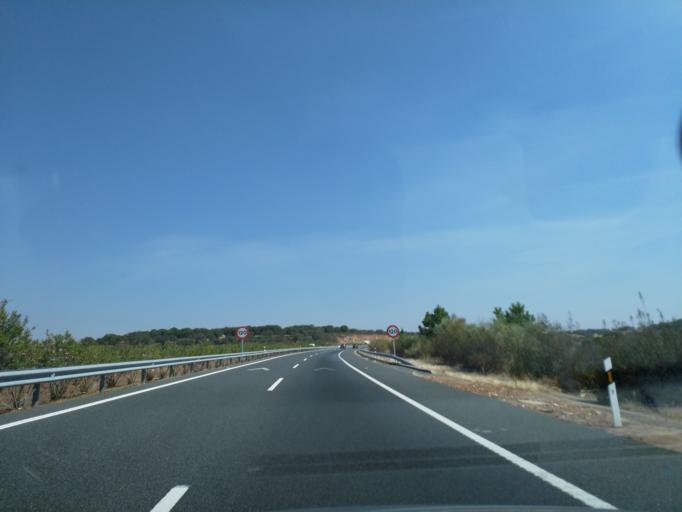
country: ES
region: Extremadura
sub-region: Provincia de Badajoz
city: Aljucen
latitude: 39.0750
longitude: -6.3122
